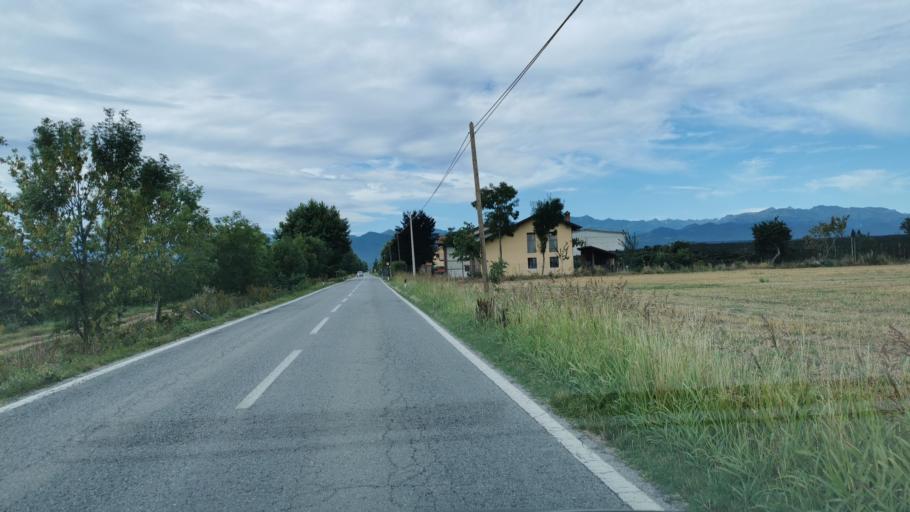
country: IT
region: Piedmont
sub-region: Provincia di Cuneo
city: Roata Rossi
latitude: 44.4691
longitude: 7.5083
